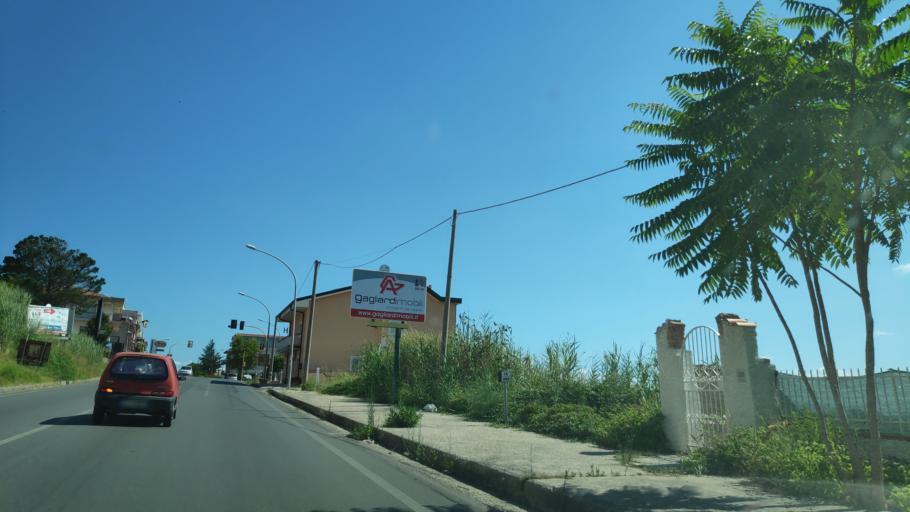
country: IT
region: Calabria
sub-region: Provincia di Cosenza
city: Campora San Giovanni
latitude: 39.0684
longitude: 16.0922
